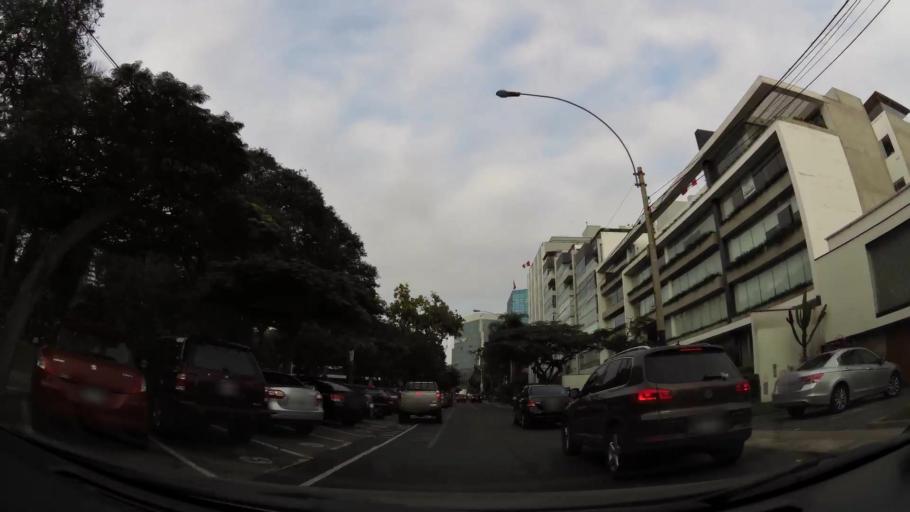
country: PE
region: Lima
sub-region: Lima
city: San Isidro
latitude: -12.1052
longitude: -77.0413
